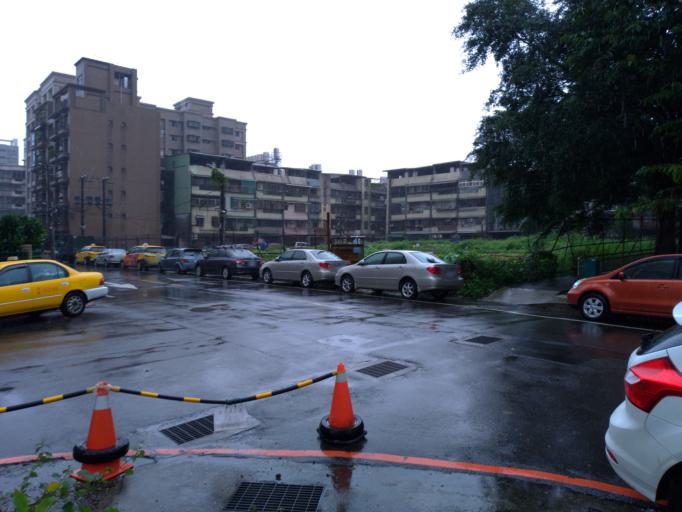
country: TW
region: Taiwan
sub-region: Keelung
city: Keelung
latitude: 25.0868
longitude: 121.6970
